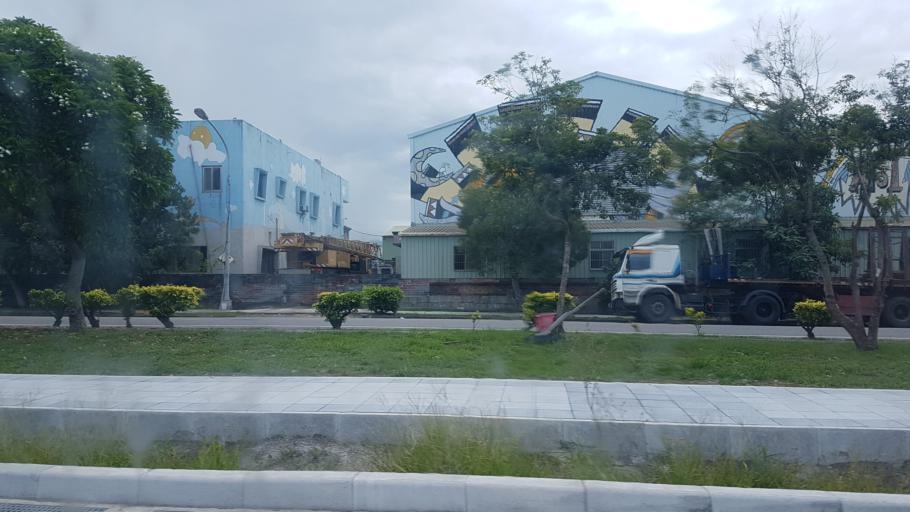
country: TW
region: Taiwan
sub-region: Hualien
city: Hualian
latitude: 23.9286
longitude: 121.5925
